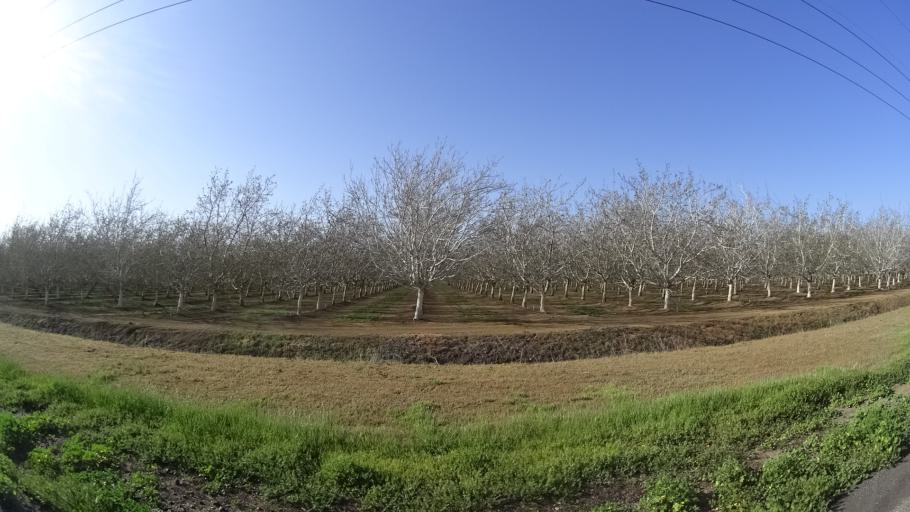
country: US
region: California
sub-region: Glenn County
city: Willows
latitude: 39.5534
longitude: -122.2197
